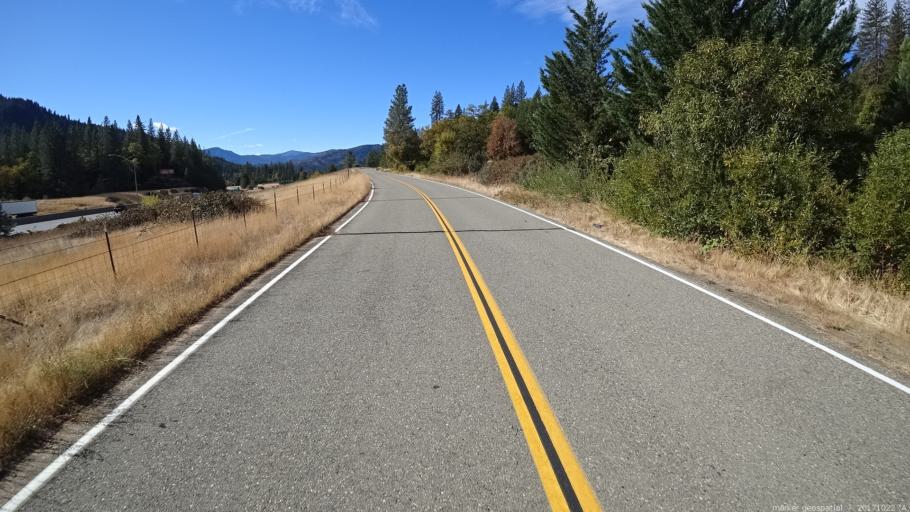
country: US
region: California
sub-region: Siskiyou County
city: Dunsmuir
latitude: 41.0016
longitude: -122.4125
